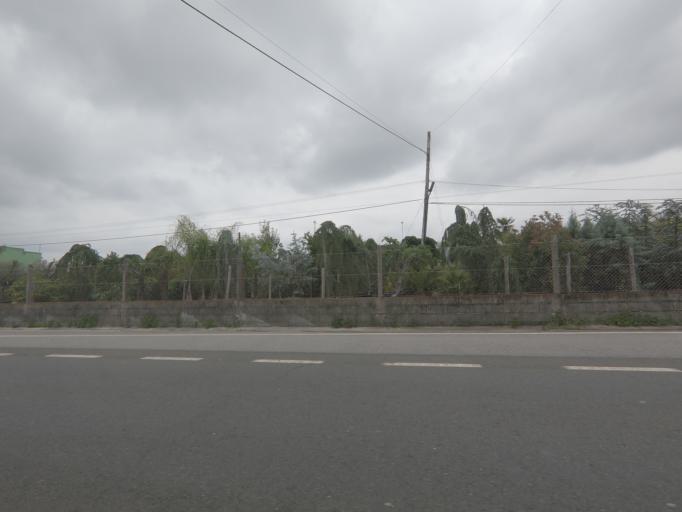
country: PT
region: Viana do Castelo
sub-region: Vila Nova de Cerveira
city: Vila Nova de Cerveira
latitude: 41.9597
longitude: -8.7635
